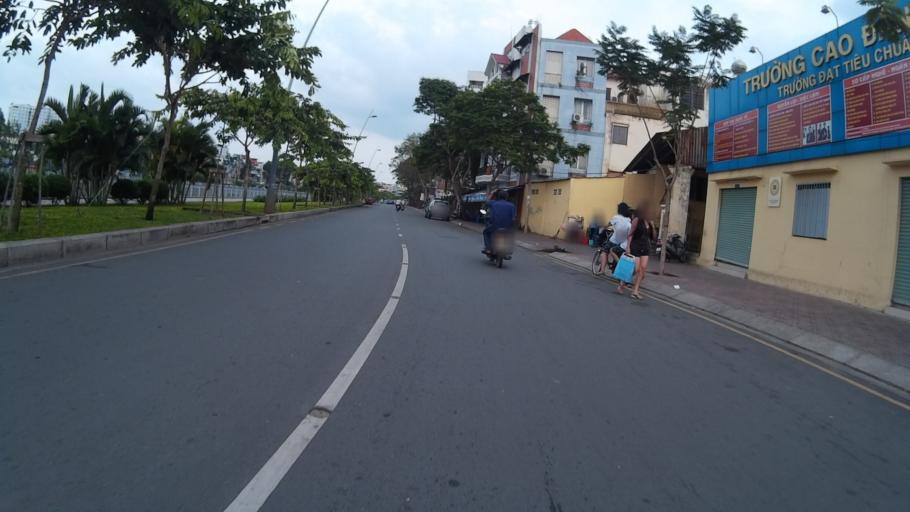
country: VN
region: Ho Chi Minh City
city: Quan Phu Nhuan
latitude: 10.7944
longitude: 106.6876
